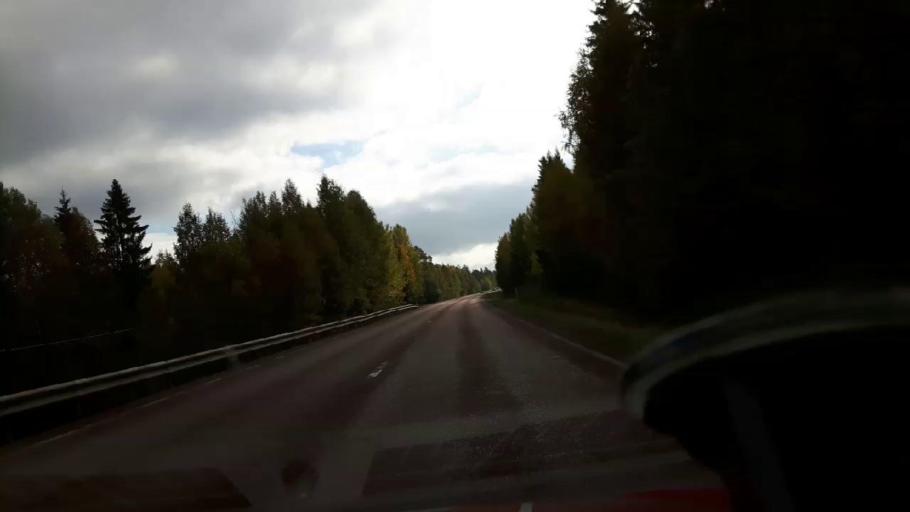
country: SE
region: Gaevleborg
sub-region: Bollnas Kommun
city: Arbra
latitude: 61.5901
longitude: 16.3073
